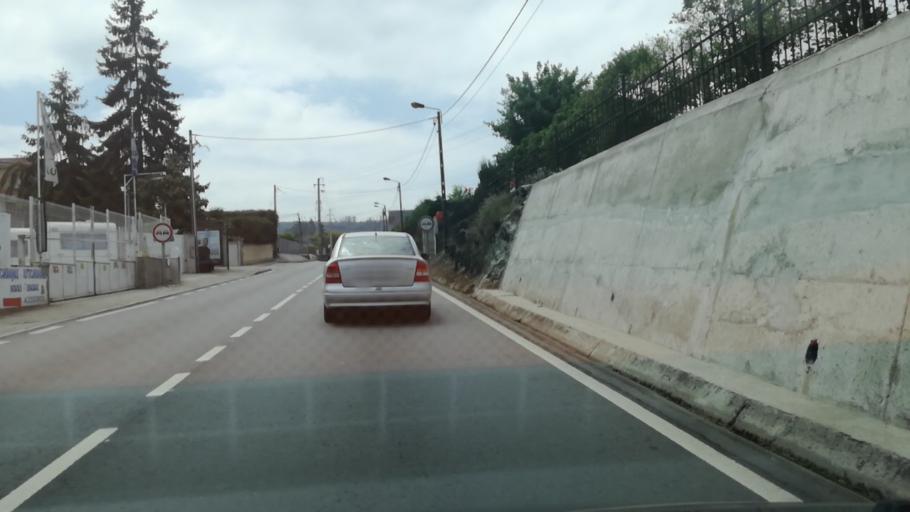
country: PT
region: Porto
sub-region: Trofa
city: Sao Romao do Coronado
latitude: 41.3142
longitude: -8.5808
